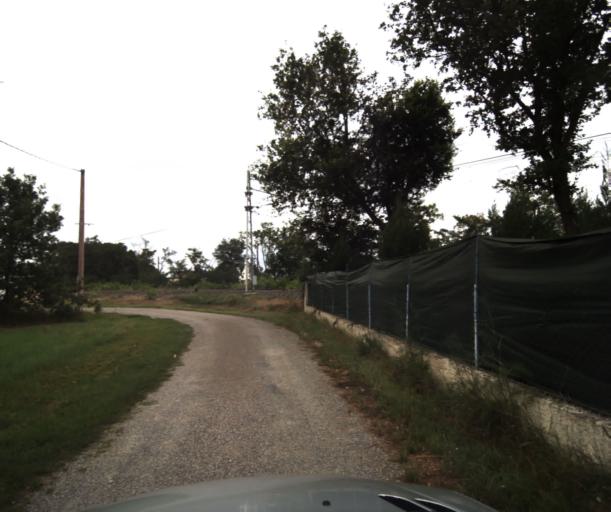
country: FR
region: Midi-Pyrenees
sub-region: Departement de la Haute-Garonne
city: Labarthe-sur-Leze
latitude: 43.4519
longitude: 1.4160
